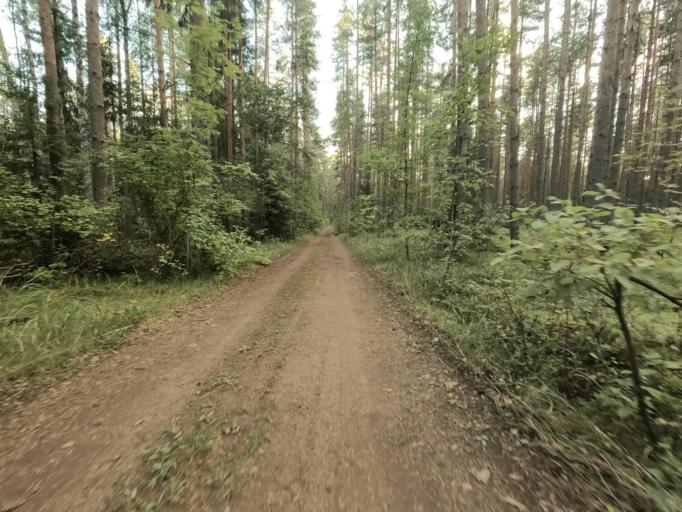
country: RU
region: Leningrad
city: Otradnoye
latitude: 59.8345
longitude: 30.7649
